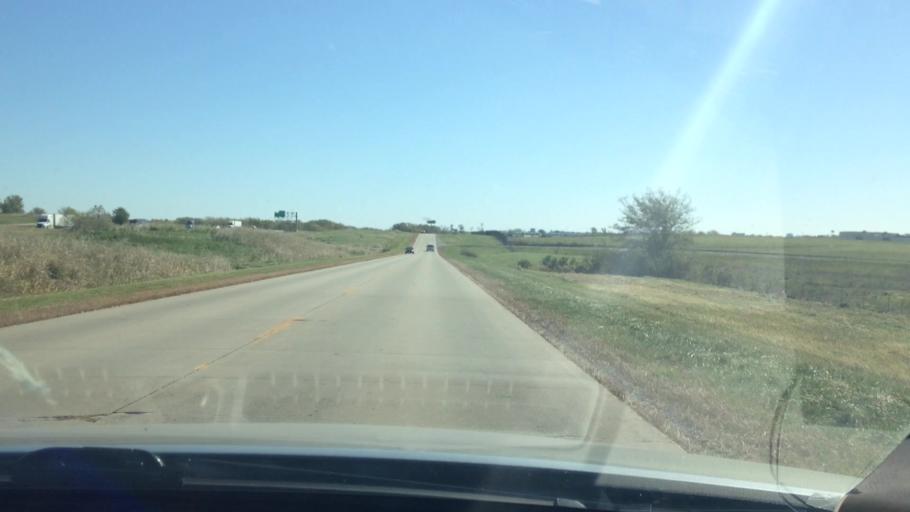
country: US
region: Missouri
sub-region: Platte County
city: Platte City
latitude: 39.3334
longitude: -94.7225
